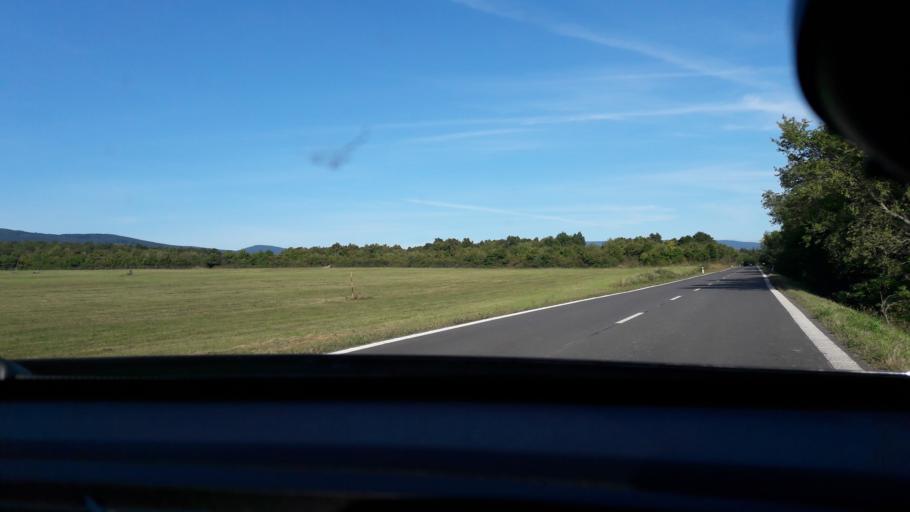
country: SK
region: Kosicky
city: Vinne
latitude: 48.8108
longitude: 22.0373
